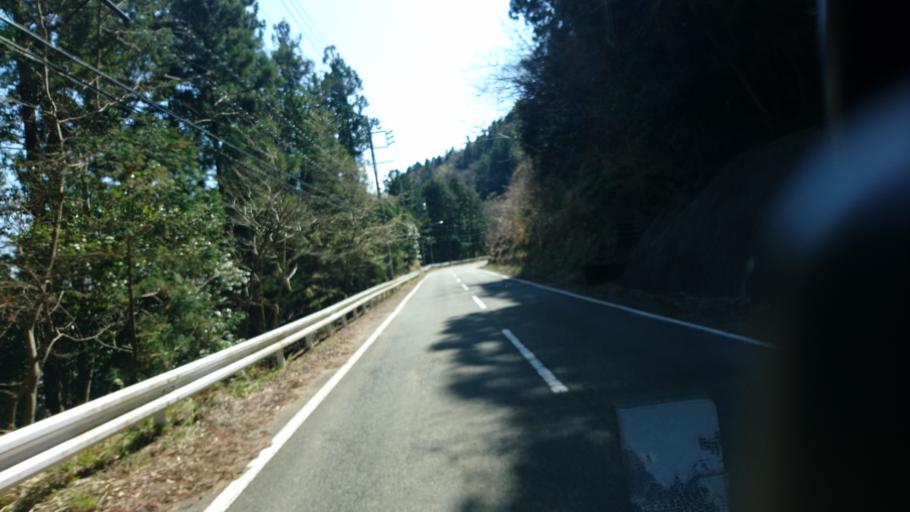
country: JP
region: Shizuoka
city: Fujinomiya
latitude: 35.3528
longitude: 138.4377
